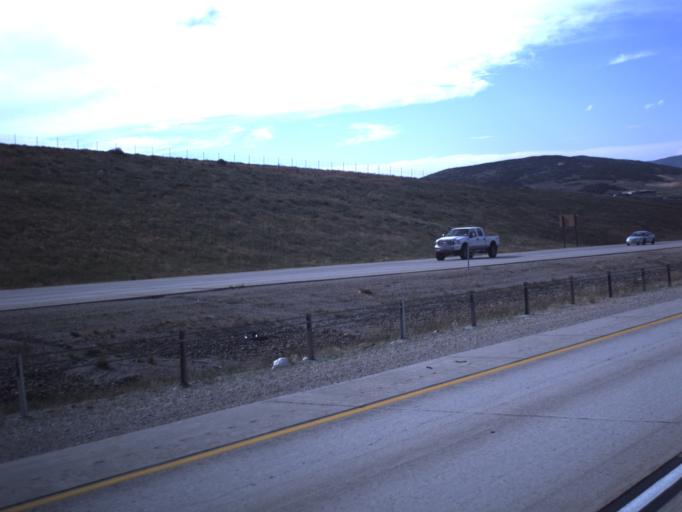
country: US
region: Utah
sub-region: Summit County
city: Park City
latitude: 40.6637
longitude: -111.4586
